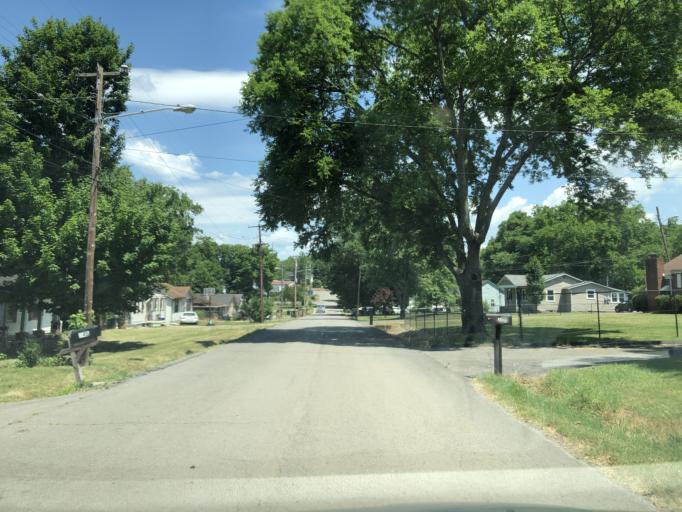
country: US
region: Tennessee
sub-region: Davidson County
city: Lakewood
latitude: 36.2611
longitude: -86.6960
